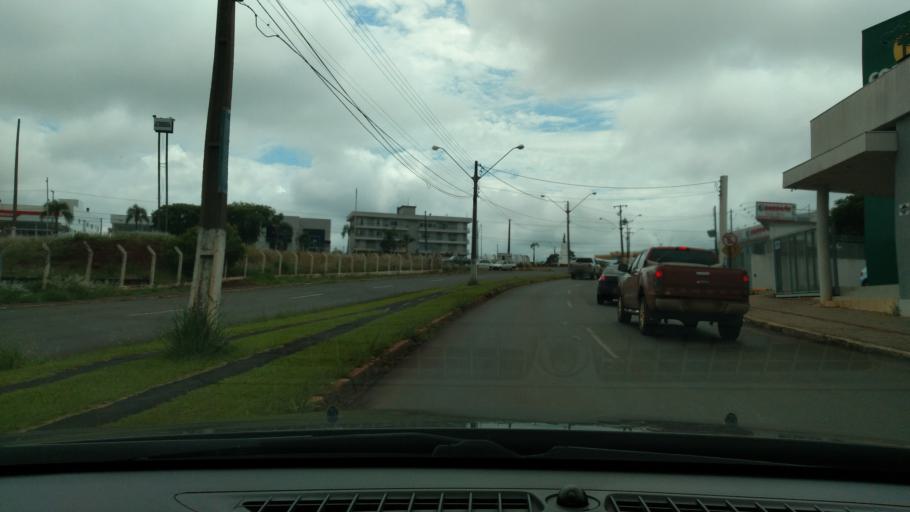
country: BR
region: Parana
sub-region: Guarapuava
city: Guarapuava
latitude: -25.3832
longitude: -51.4694
